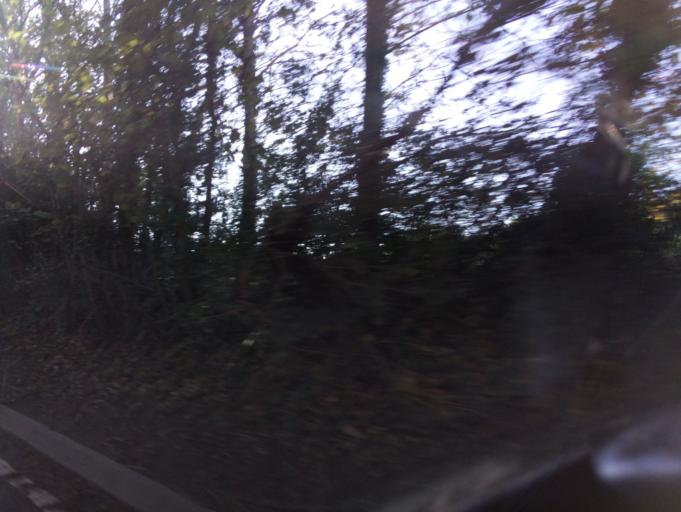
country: GB
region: England
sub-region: Dorset
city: Sherborne
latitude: 50.8435
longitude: -2.4617
